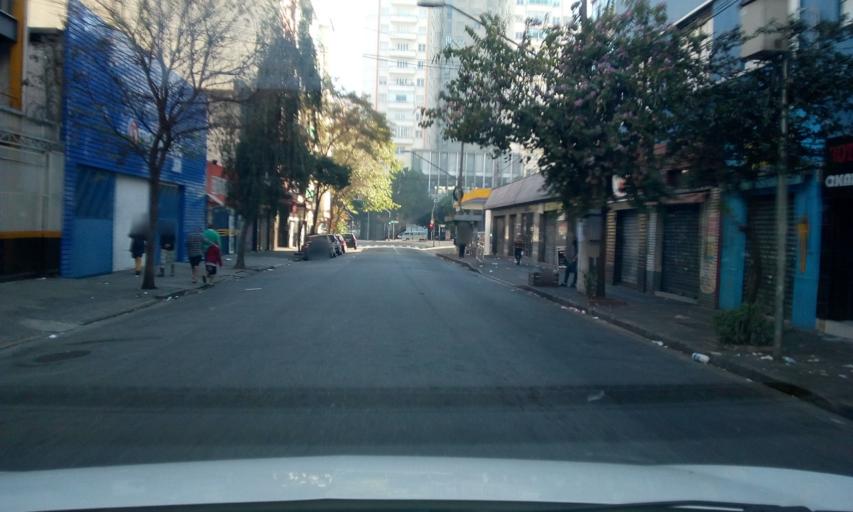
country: BR
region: Sao Paulo
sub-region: Sao Paulo
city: Sao Paulo
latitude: -23.5427
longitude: -46.6464
